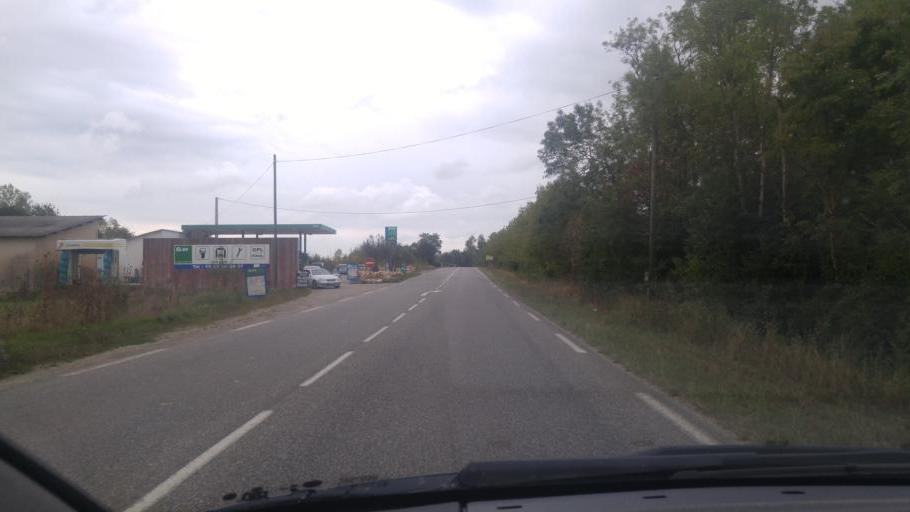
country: FR
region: Midi-Pyrenees
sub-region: Departement du Gers
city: Lectoure
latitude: 43.9172
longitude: 0.6274
